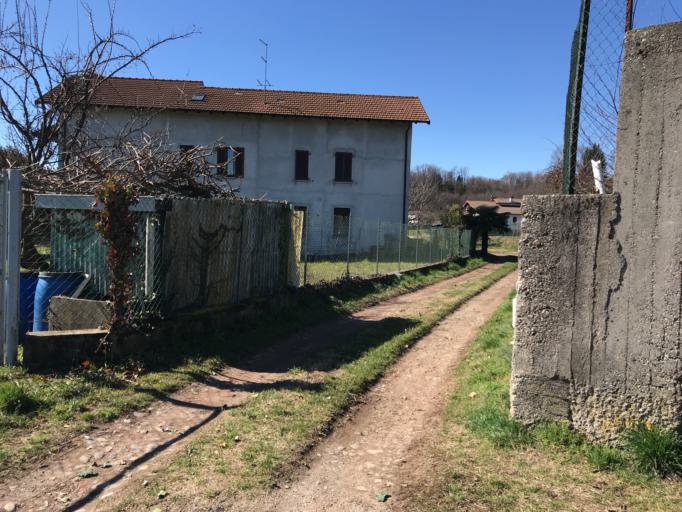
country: IT
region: Lombardy
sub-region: Provincia di Varese
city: Angera
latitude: 45.7816
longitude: 8.5871
